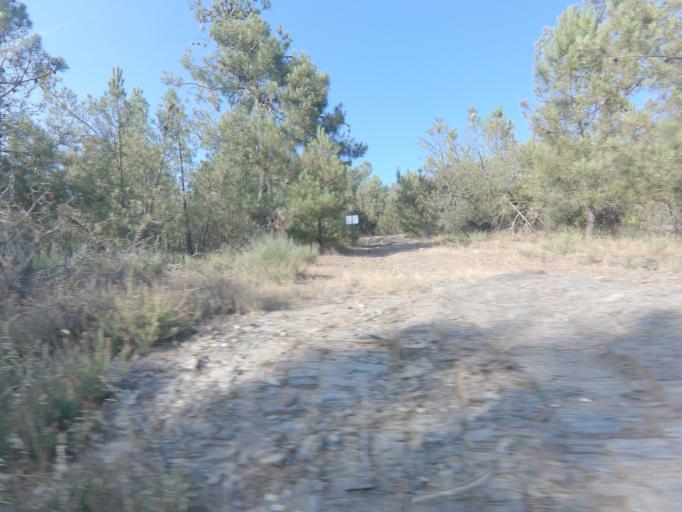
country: PT
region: Vila Real
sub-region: Sabrosa
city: Vilela
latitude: 41.1894
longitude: -7.6197
